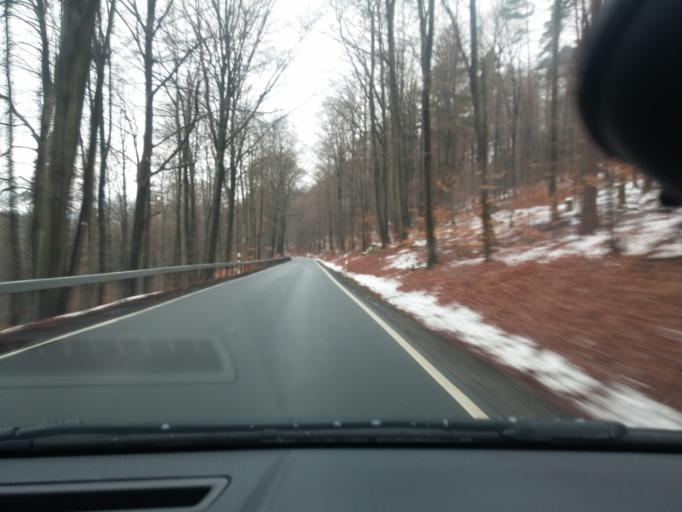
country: DE
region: Hesse
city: Michelstadt
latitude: 49.6882
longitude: 9.0310
